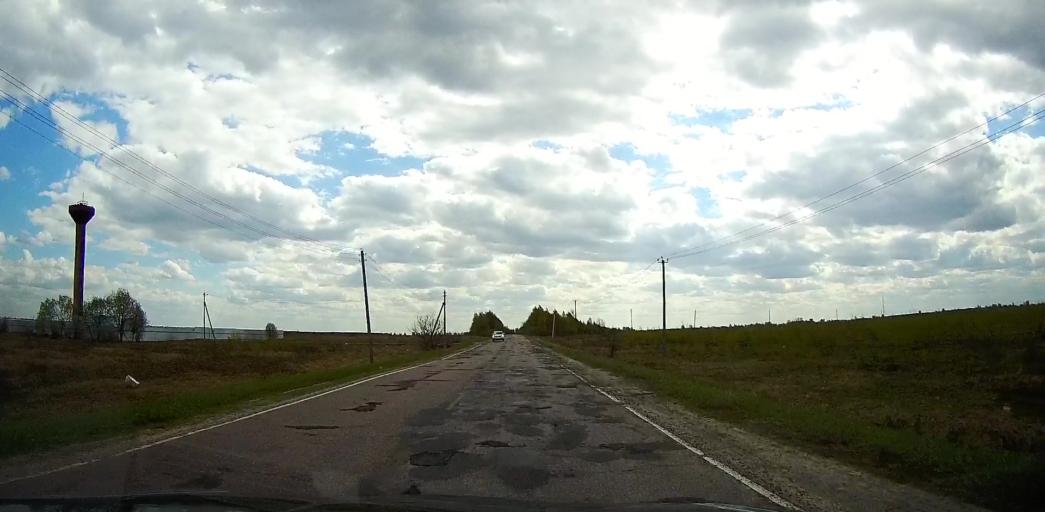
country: RU
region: Moskovskaya
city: Davydovo
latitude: 55.6397
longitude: 38.7485
